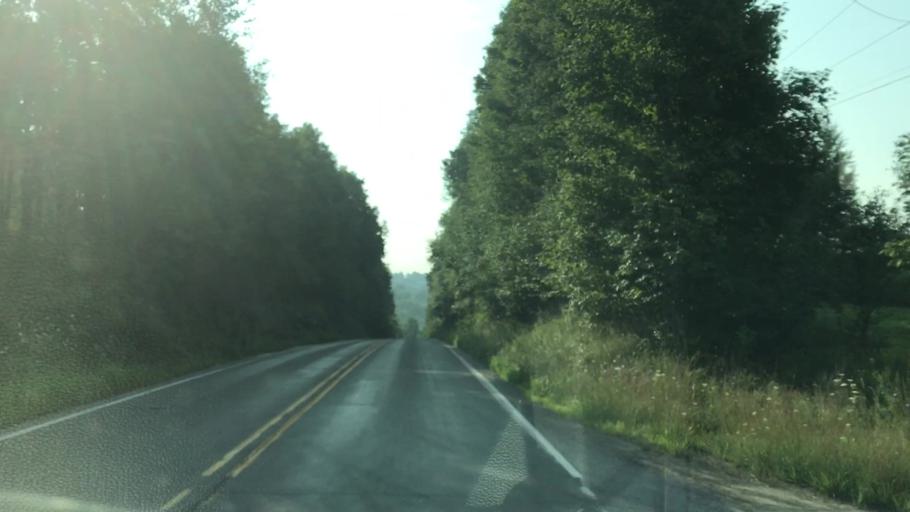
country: US
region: Pennsylvania
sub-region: Lackawanna County
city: Dalton
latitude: 41.5989
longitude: -75.6785
